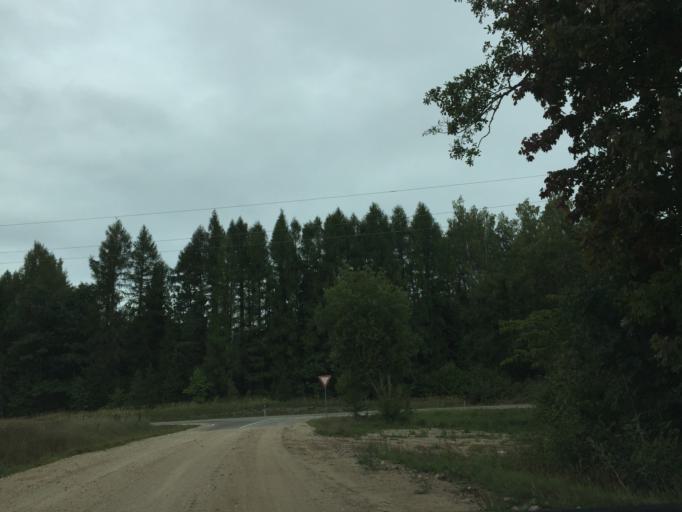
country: LV
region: Limbazu Rajons
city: Limbazi
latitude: 57.5269
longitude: 24.9112
